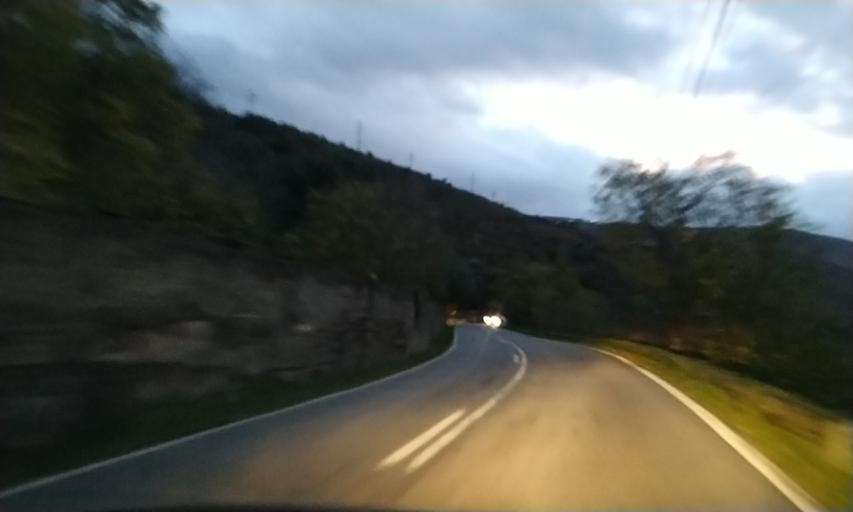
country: PT
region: Viseu
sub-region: Tabuaco
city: Tabuaco
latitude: 41.1804
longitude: -7.5502
